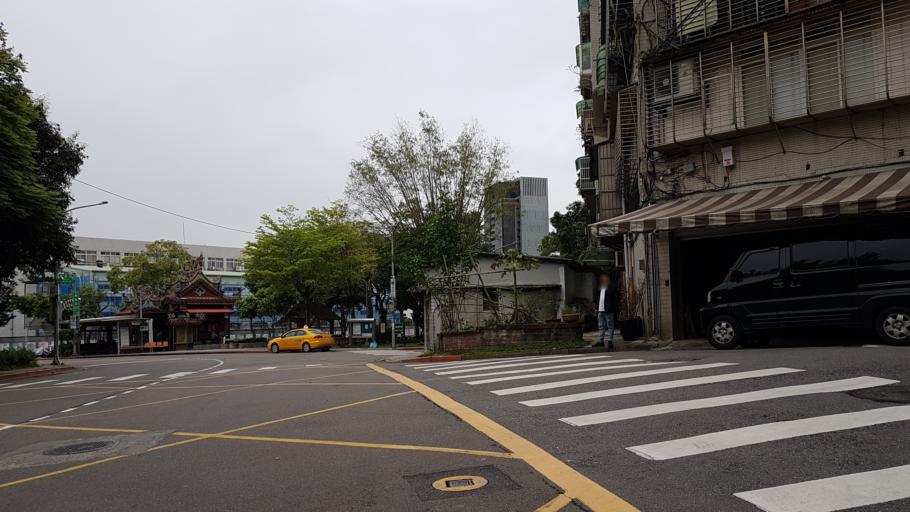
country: TW
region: Taipei
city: Taipei
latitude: 25.0453
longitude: 121.5928
